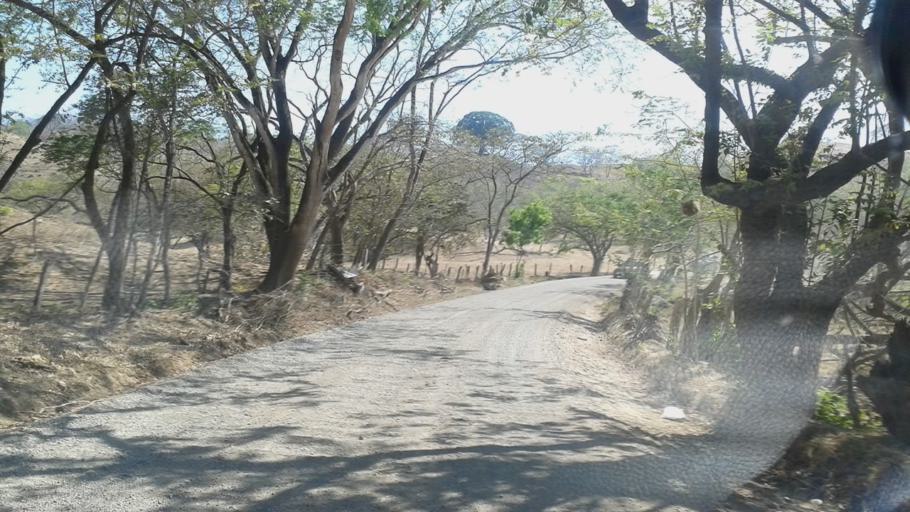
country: CR
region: Guanacaste
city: Santa Cruz
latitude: 10.1854
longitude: -85.7695
